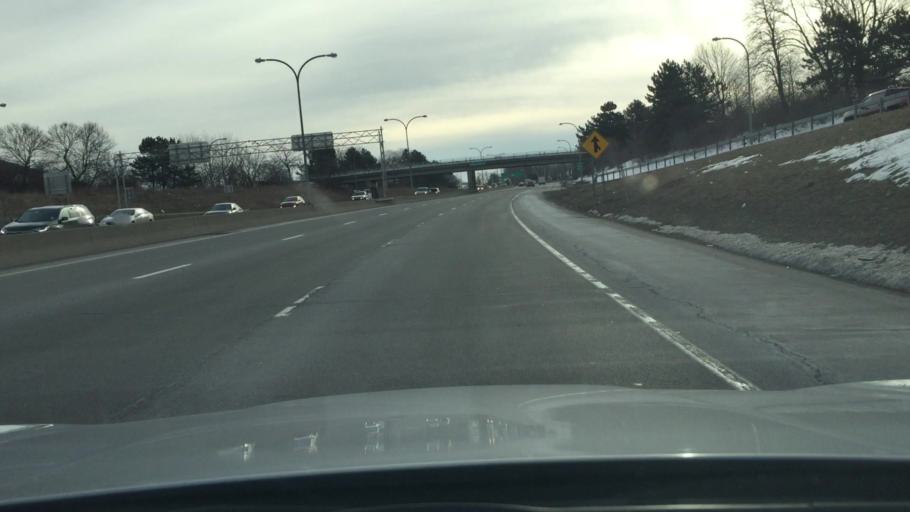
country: US
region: New York
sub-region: Erie County
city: Eggertsville
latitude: 42.9331
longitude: -78.7982
